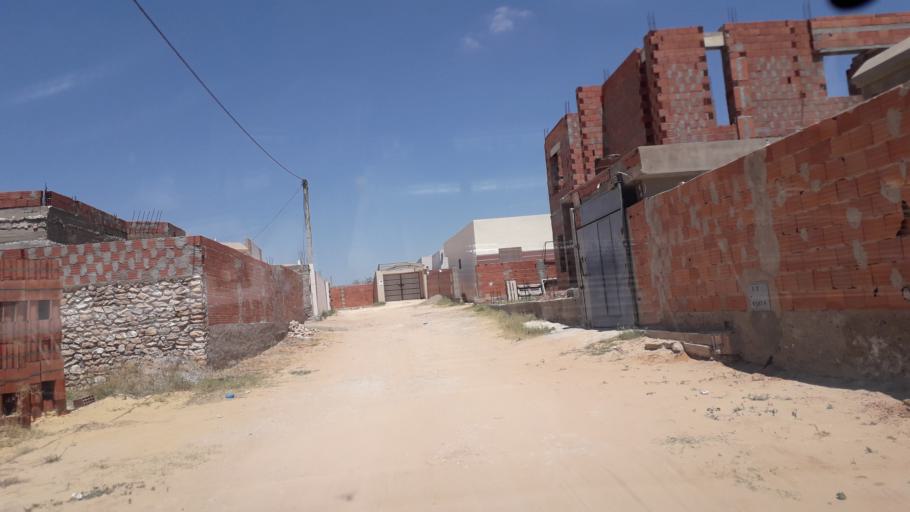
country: TN
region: Safaqis
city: Al Qarmadah
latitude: 34.8301
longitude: 10.7757
